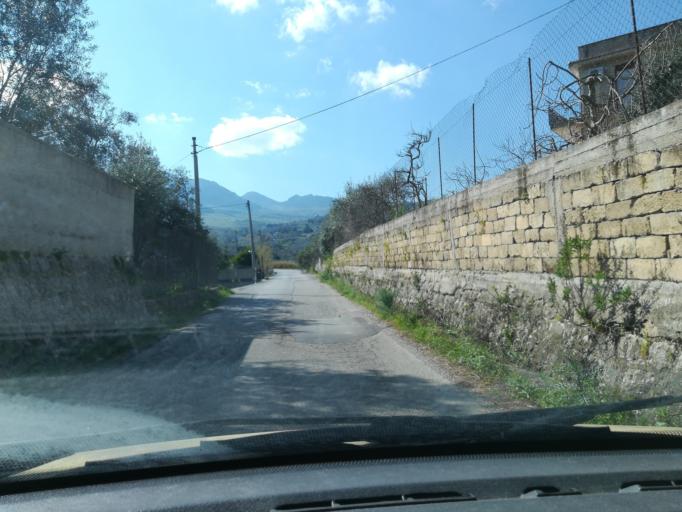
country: IT
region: Sicily
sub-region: Palermo
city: Cannizzaro-Favara
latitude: 38.0478
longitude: 13.2613
